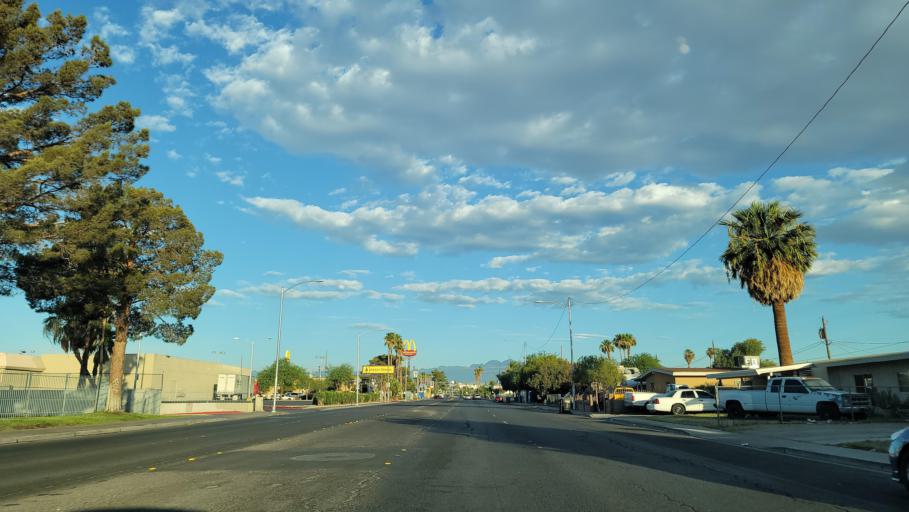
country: US
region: Nevada
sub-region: Clark County
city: North Las Vegas
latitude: 36.1885
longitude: -115.1128
